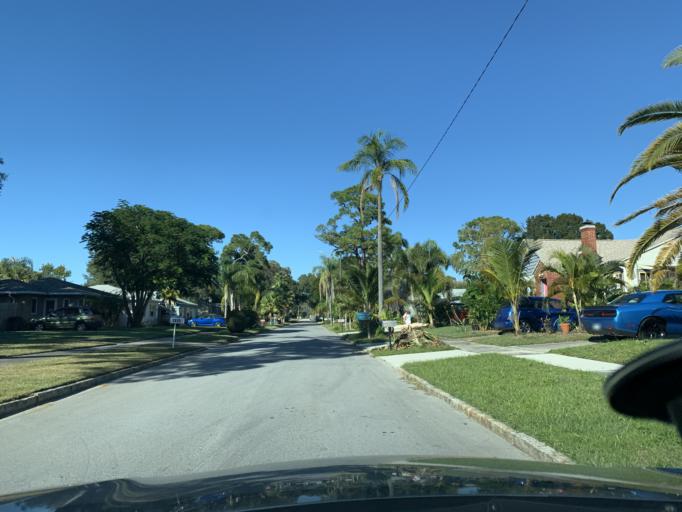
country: US
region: Florida
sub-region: Pinellas County
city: Gulfport
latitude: 27.7417
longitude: -82.6980
